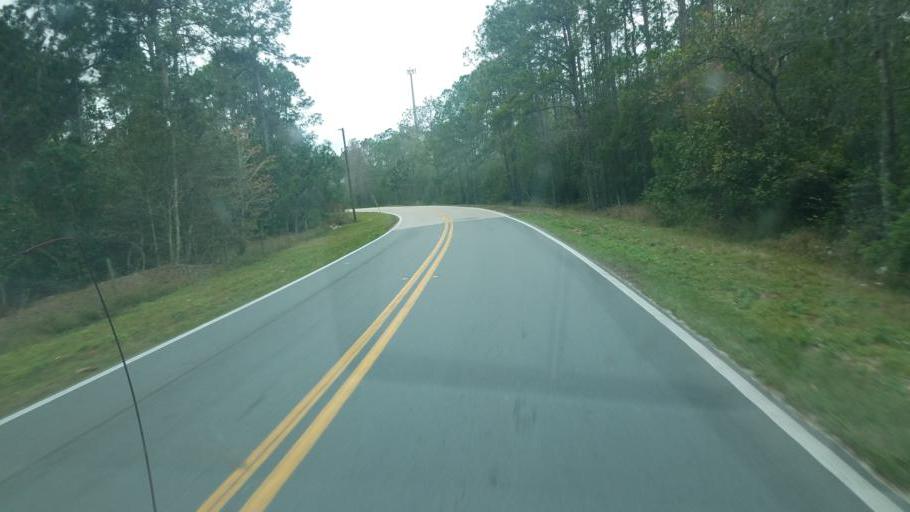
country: US
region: Florida
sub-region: Lake County
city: Four Corners
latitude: 28.2590
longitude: -81.7322
